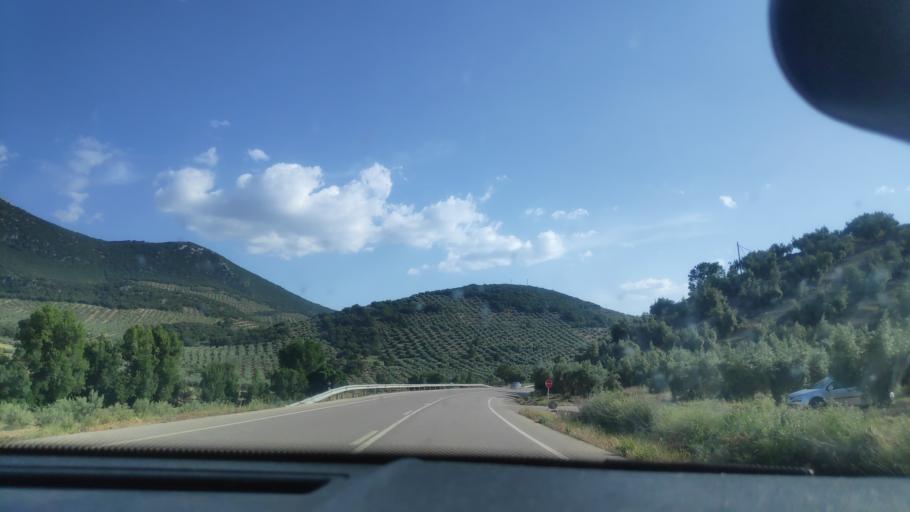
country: ES
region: Andalusia
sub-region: Provincia de Granada
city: Benalua de las Villas
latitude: 37.4415
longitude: -3.6523
